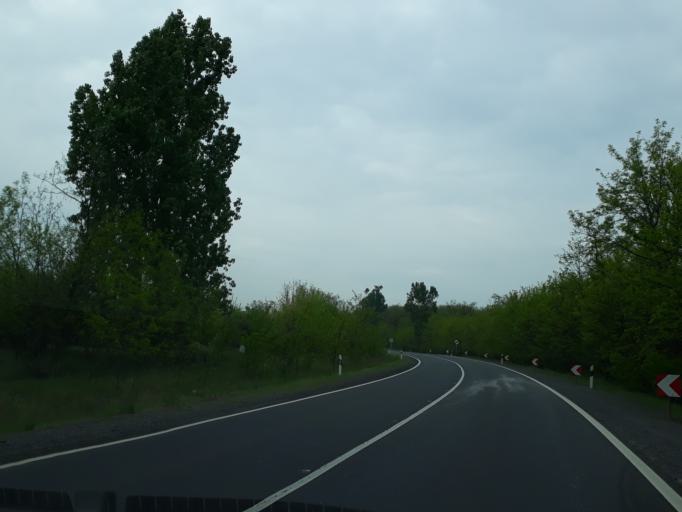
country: HU
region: Szabolcs-Szatmar-Bereg
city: Nyirtass
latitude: 48.1160
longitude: 21.9924
